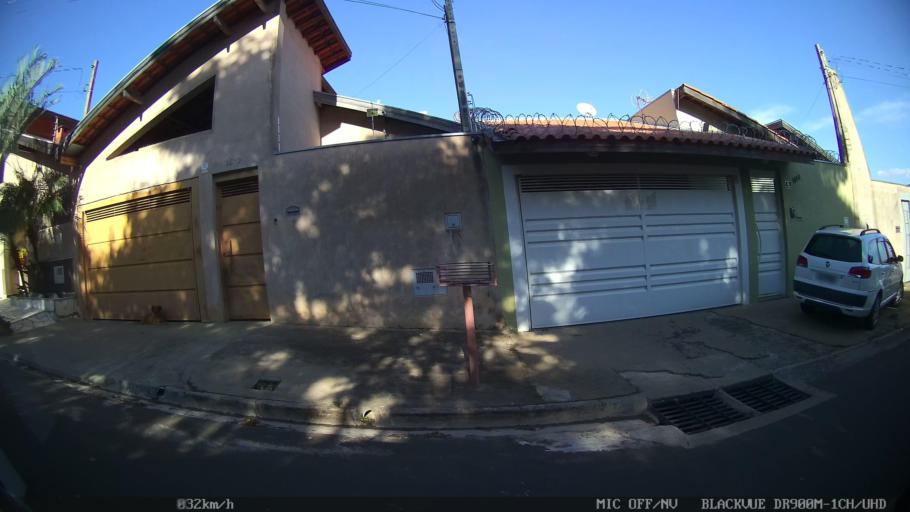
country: BR
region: Sao Paulo
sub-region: Franca
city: Franca
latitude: -20.5127
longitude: -47.4280
